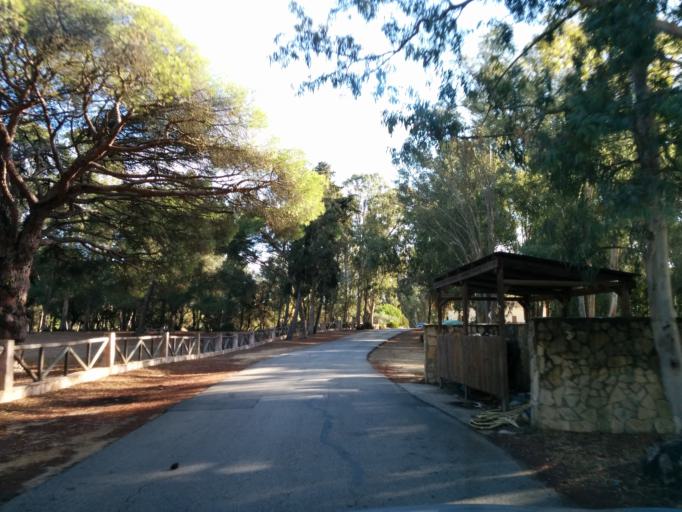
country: ES
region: Andalusia
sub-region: Provincia de Cadiz
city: Vejer de la Frontera
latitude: 36.1981
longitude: -5.9816
